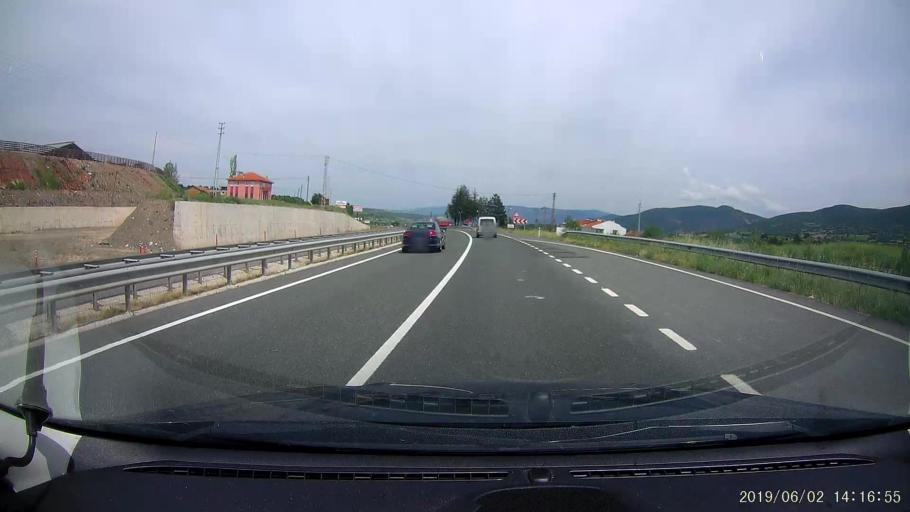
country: TR
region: Kastamonu
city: Tosya
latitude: 40.9508
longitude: 33.9208
